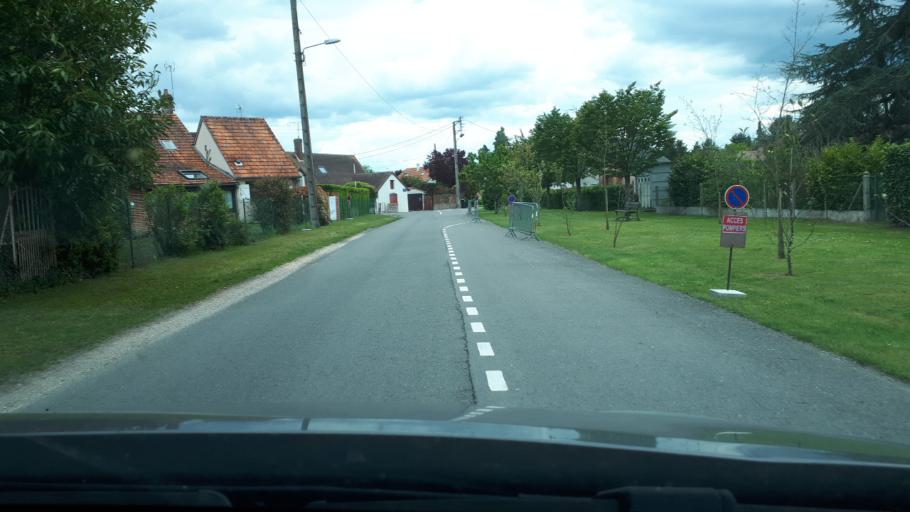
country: FR
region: Centre
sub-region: Departement du Loir-et-Cher
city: Souesmes
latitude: 47.5122
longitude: 2.1499
